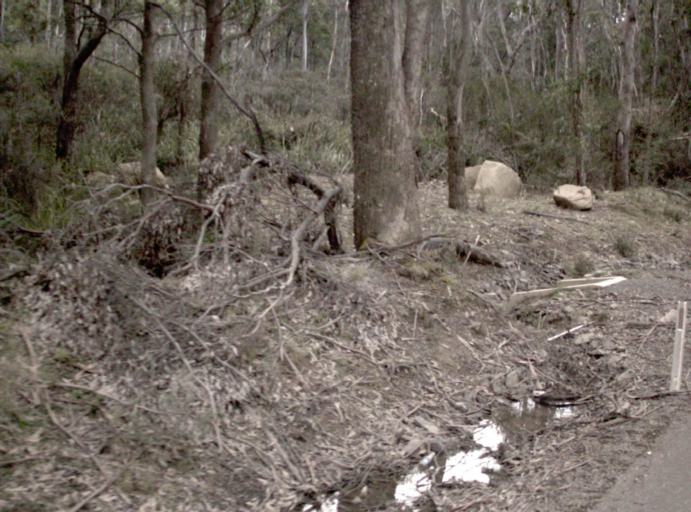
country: AU
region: Tasmania
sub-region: Launceston
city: Mayfield
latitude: -41.3521
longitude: 147.2205
